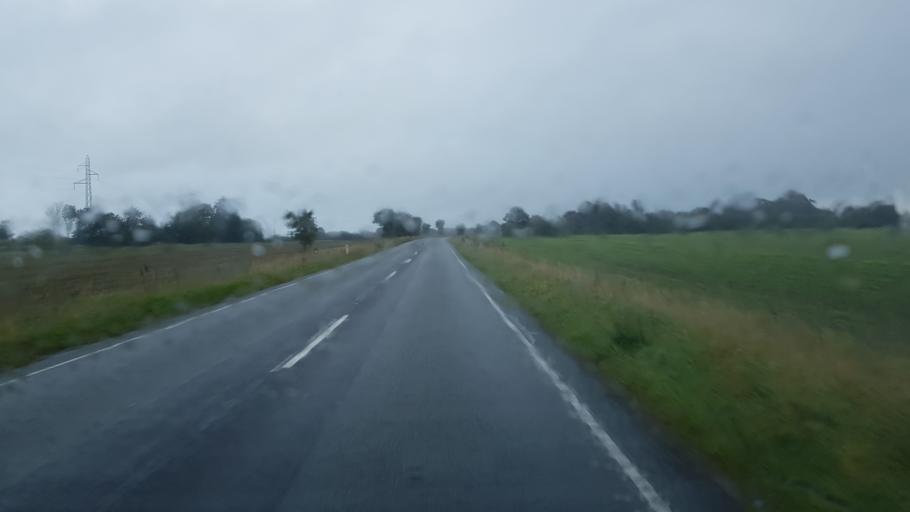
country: DK
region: South Denmark
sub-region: Kolding Kommune
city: Vamdrup
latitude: 55.3497
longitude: 9.2371
